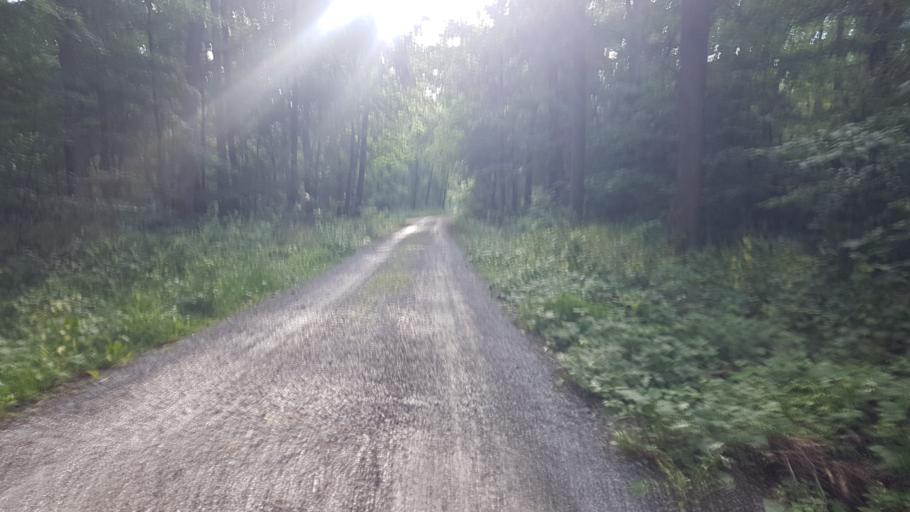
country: DE
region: Baden-Wuerttemberg
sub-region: Regierungsbezirk Stuttgart
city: Zaberfeld
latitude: 49.0372
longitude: 8.9243
